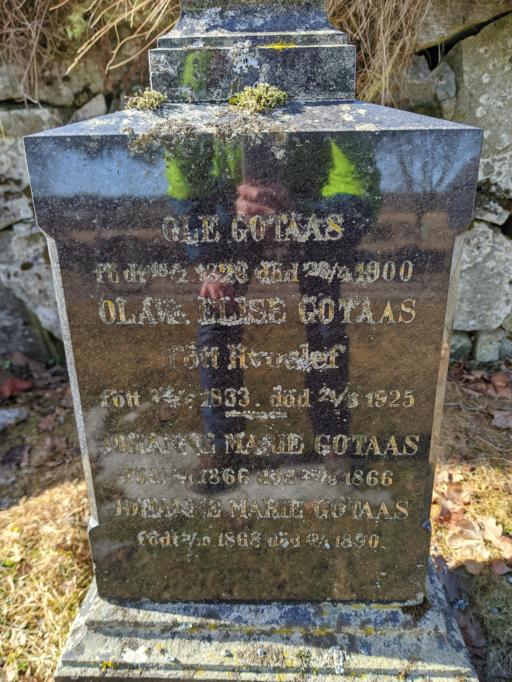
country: NO
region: Akershus
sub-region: Ullensaker
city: Jessheim
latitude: 60.1428
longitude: 11.1268
